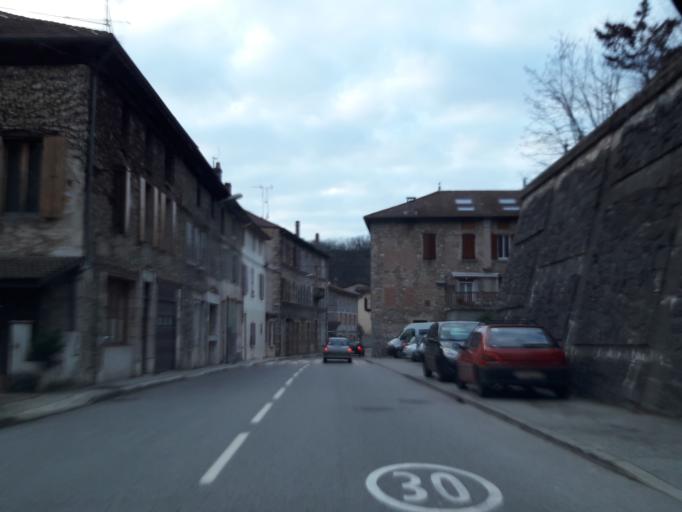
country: FR
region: Rhone-Alpes
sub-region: Departement de l'Isere
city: Pont-en-Royans
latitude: 45.0622
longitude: 5.3418
